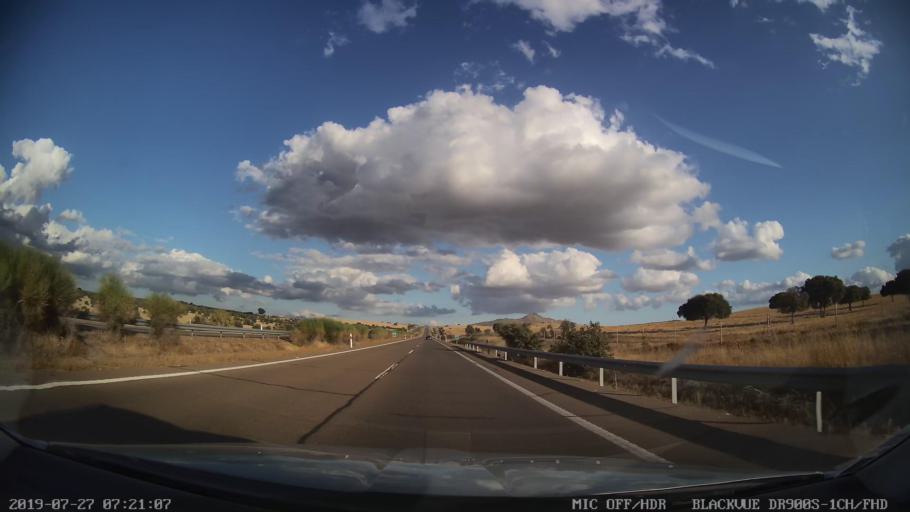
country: ES
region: Extremadura
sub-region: Provincia de Caceres
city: Santa Cruz de la Sierra
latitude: 39.3678
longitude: -5.8745
